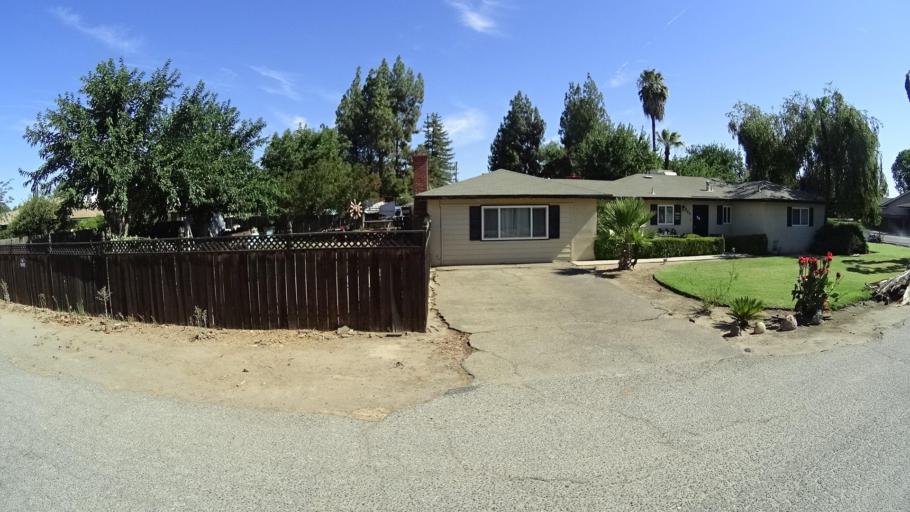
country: US
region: California
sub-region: Fresno County
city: Sunnyside
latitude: 36.7449
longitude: -119.7052
